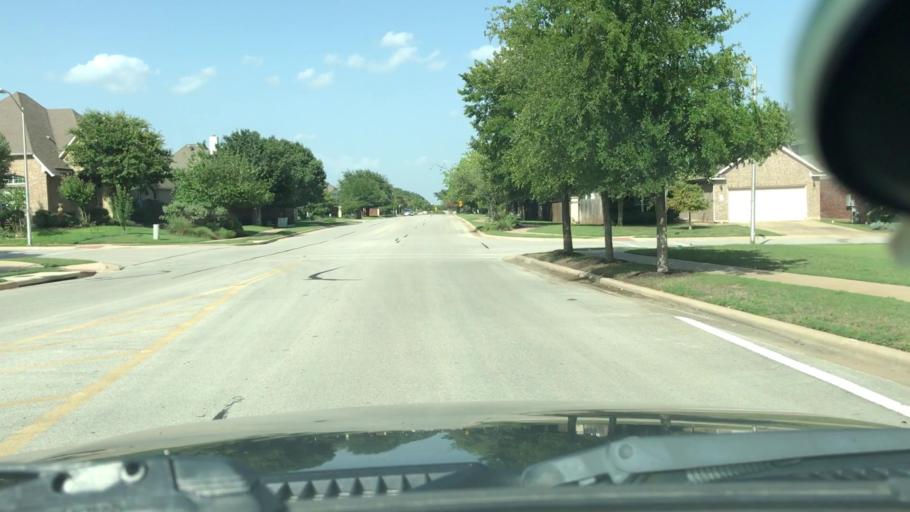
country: US
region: Texas
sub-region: Williamson County
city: Leander
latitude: 30.5387
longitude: -97.8596
